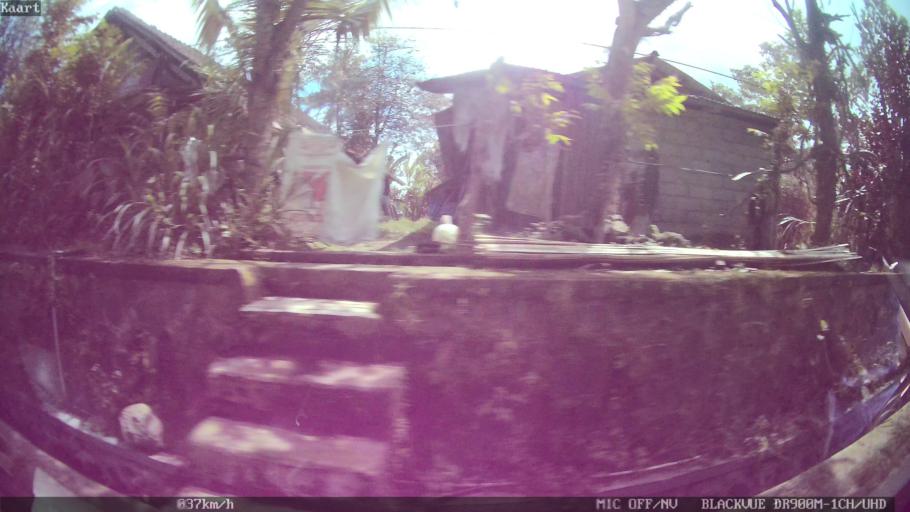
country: ID
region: Bali
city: Banjar Abuan
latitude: -8.4635
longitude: 115.3409
